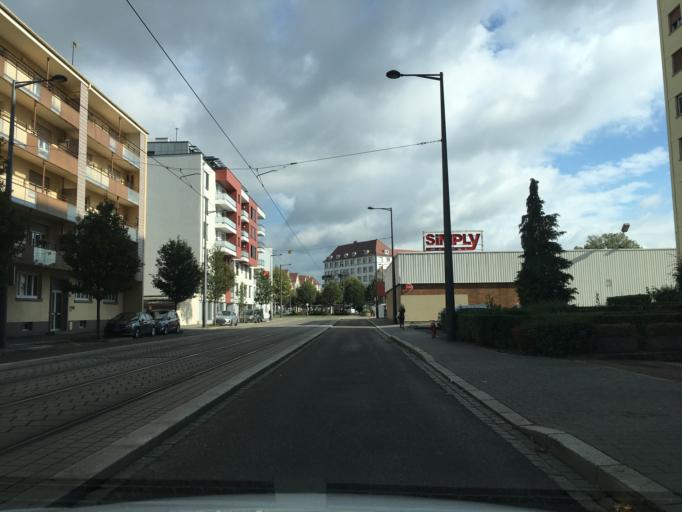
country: FR
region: Alsace
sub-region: Departement du Bas-Rhin
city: Strasbourg
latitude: 48.5657
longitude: 7.7718
